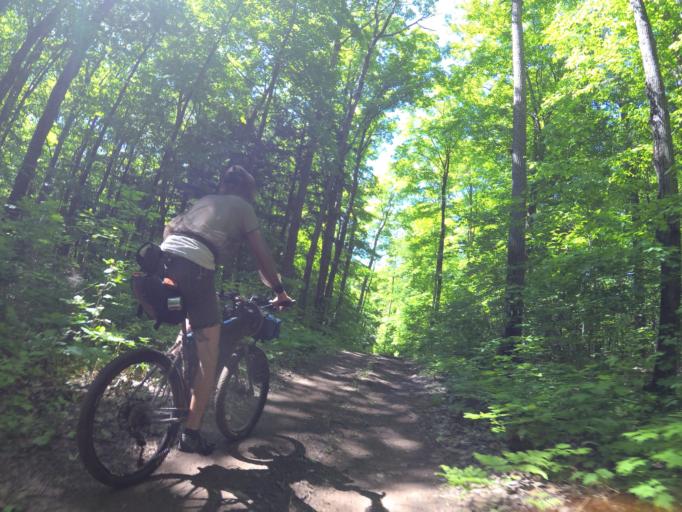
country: CA
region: Ontario
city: Renfrew
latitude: 45.0582
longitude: -77.0834
